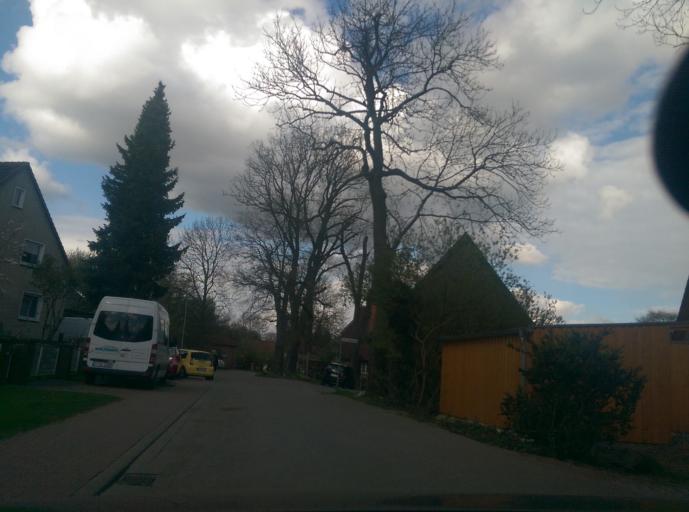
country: DE
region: Lower Saxony
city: Lindwedel
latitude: 52.5511
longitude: 9.6776
